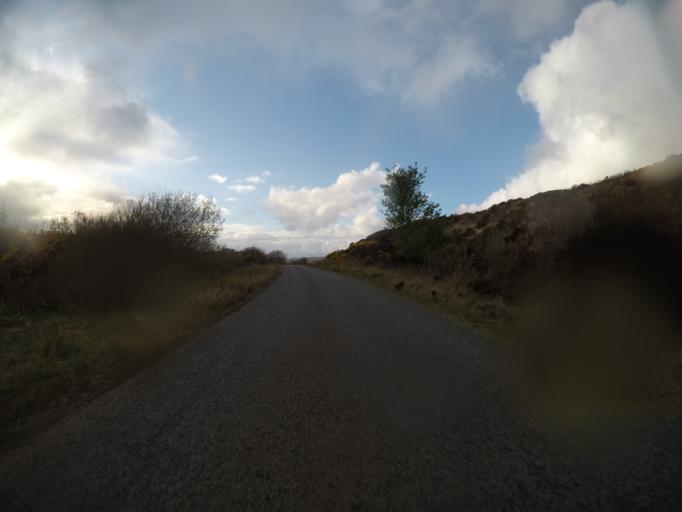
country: GB
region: Scotland
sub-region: Highland
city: Isle of Skye
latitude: 57.4688
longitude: -6.2990
